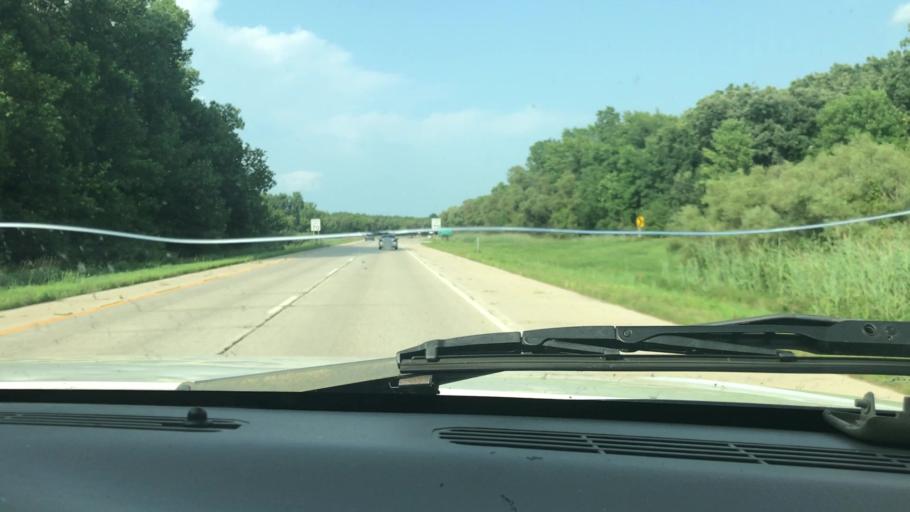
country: US
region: Wisconsin
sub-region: Brown County
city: Green Bay
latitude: 44.5209
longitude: -87.9508
